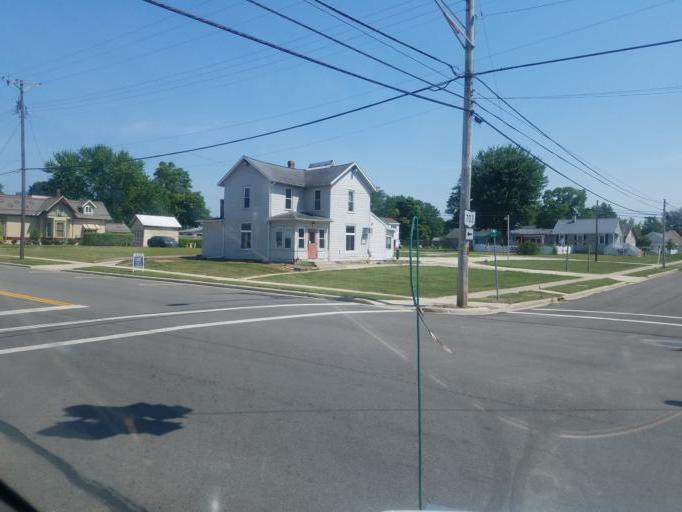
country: US
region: Ohio
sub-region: Mercer County
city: Celina
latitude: 40.4892
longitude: -84.5496
